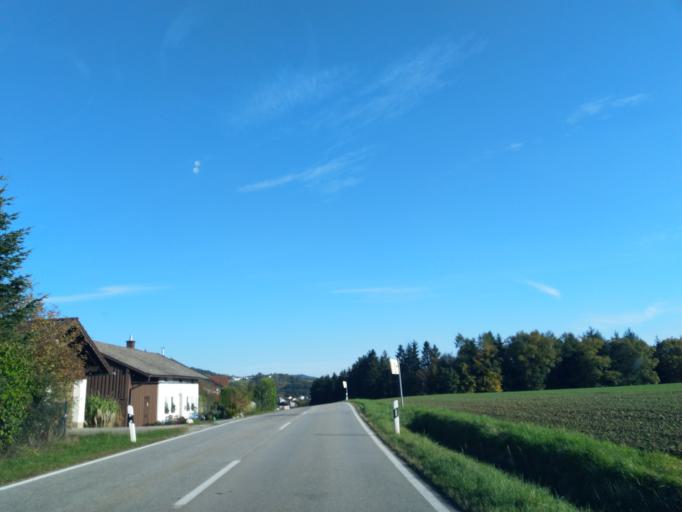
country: DE
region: Bavaria
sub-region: Lower Bavaria
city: Metten
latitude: 48.8891
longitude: 12.9115
